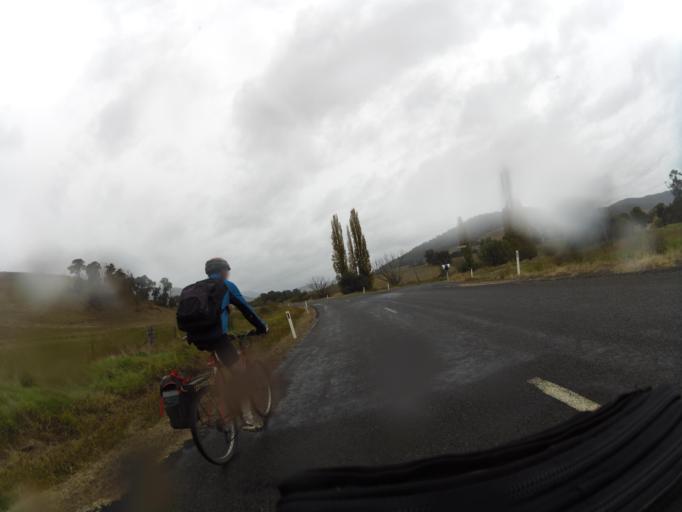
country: AU
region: New South Wales
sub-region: Greater Hume Shire
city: Holbrook
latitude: -36.2384
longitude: 147.6452
